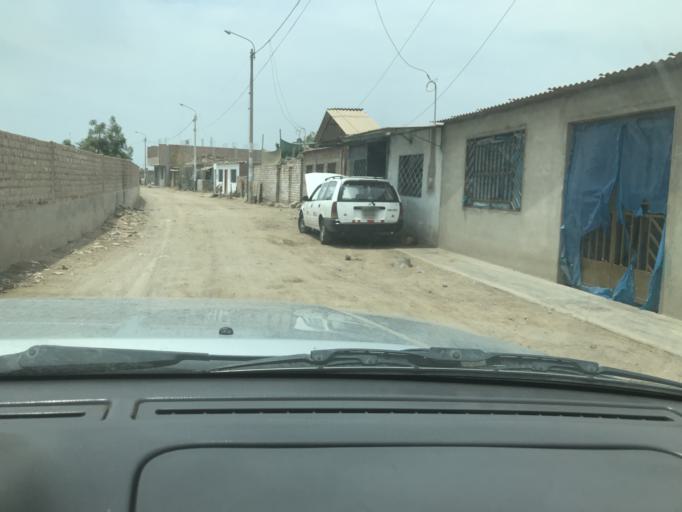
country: PE
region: La Libertad
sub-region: Viru
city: Viru
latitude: -8.4182
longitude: -78.7877
